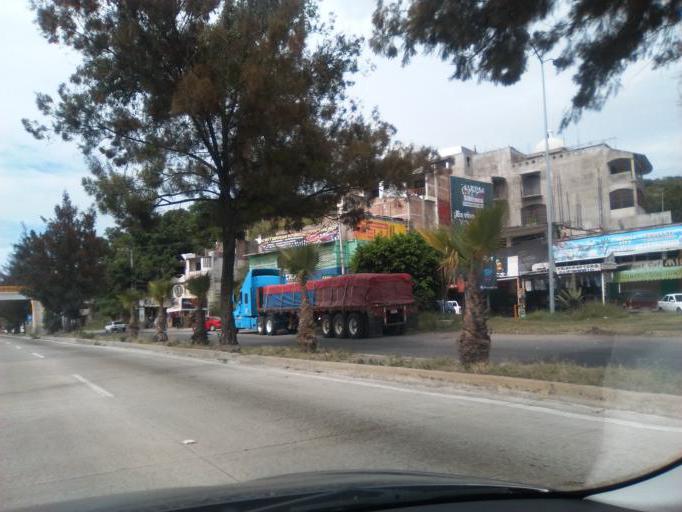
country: MX
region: Guerrero
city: Chilpancingo de los Bravos
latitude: 17.5688
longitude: -99.5116
